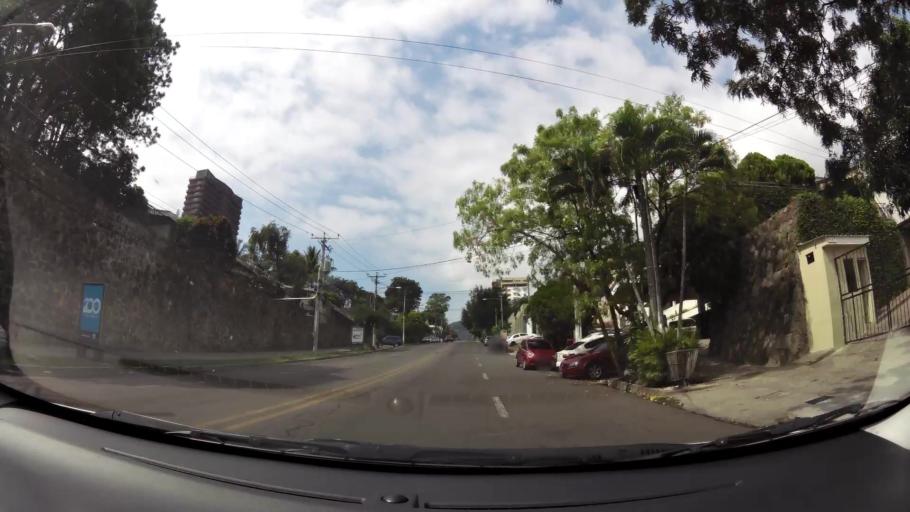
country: SV
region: La Libertad
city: Santa Tecla
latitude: 13.7040
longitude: -89.2537
